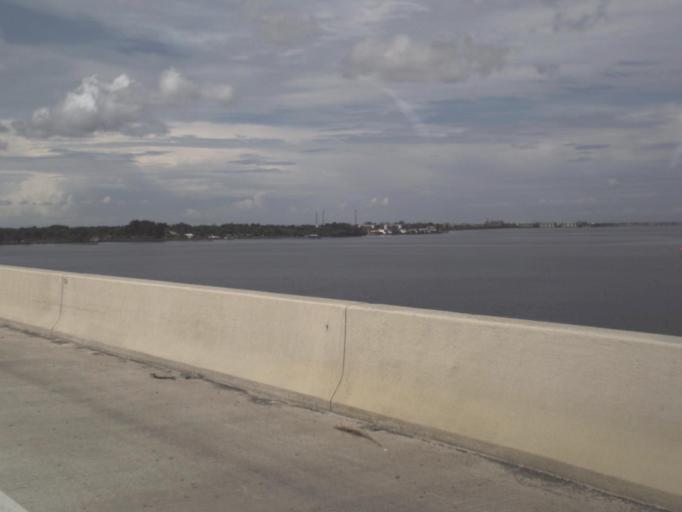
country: US
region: Florida
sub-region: Charlotte County
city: Harbour Heights
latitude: 26.9603
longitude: -82.0203
